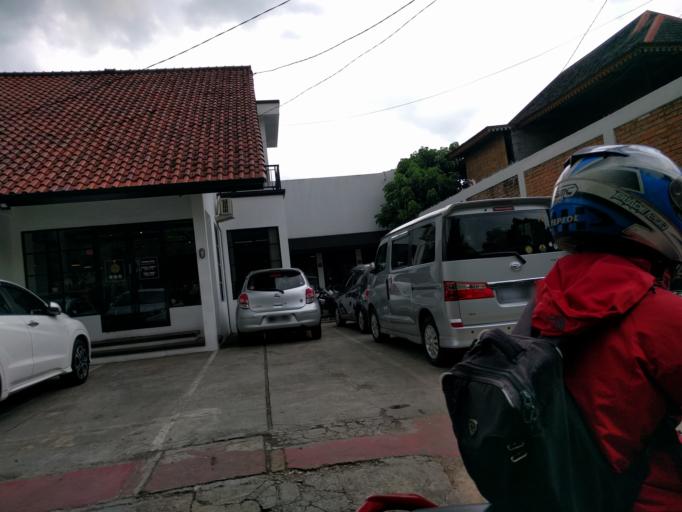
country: ID
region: West Java
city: Bogor
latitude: -6.5885
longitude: 106.8166
